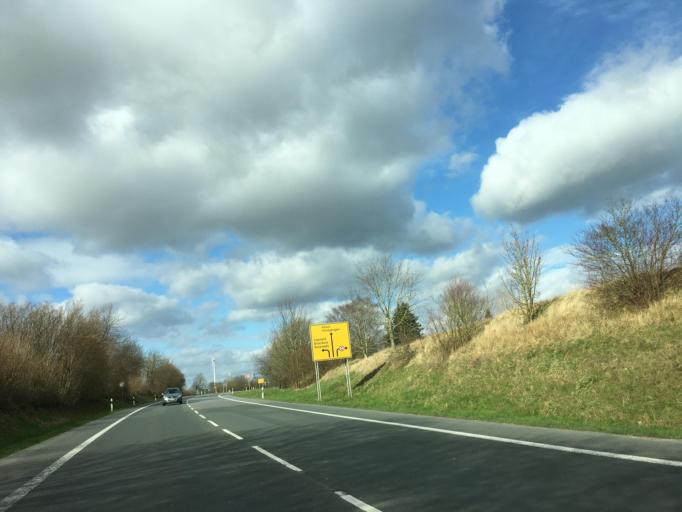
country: DE
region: North Rhine-Westphalia
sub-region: Regierungsbezirk Munster
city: Horstmar
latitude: 52.0760
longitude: 7.2973
